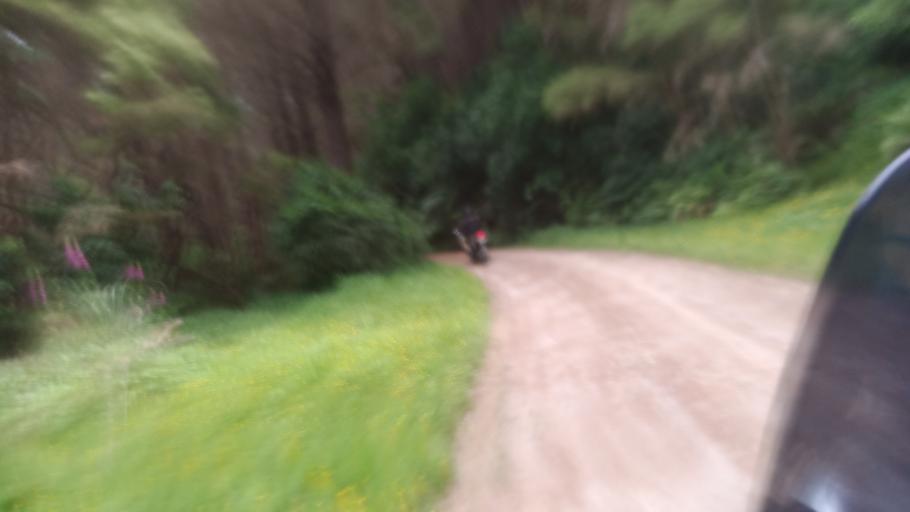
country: NZ
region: Gisborne
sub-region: Gisborne District
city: Gisborne
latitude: -38.4578
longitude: 177.9105
